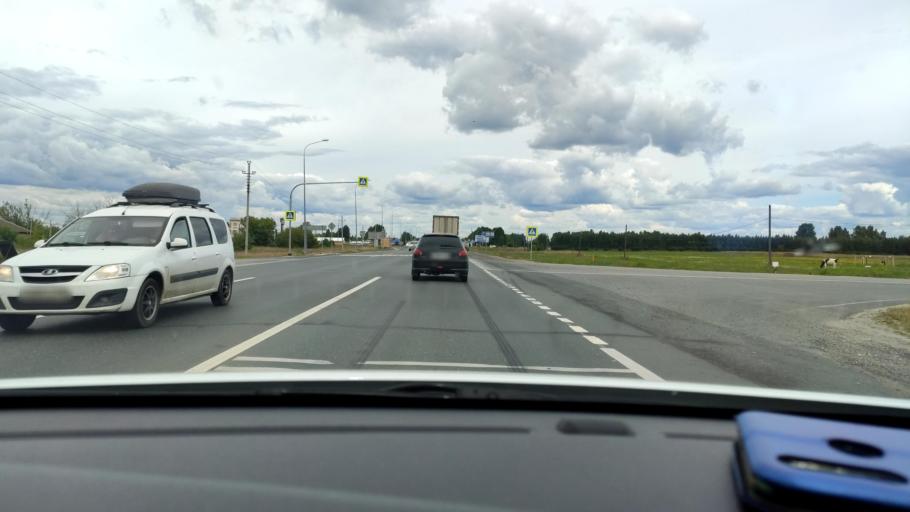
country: RU
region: Mariy-El
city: Pomary
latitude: 55.9641
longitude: 48.3664
